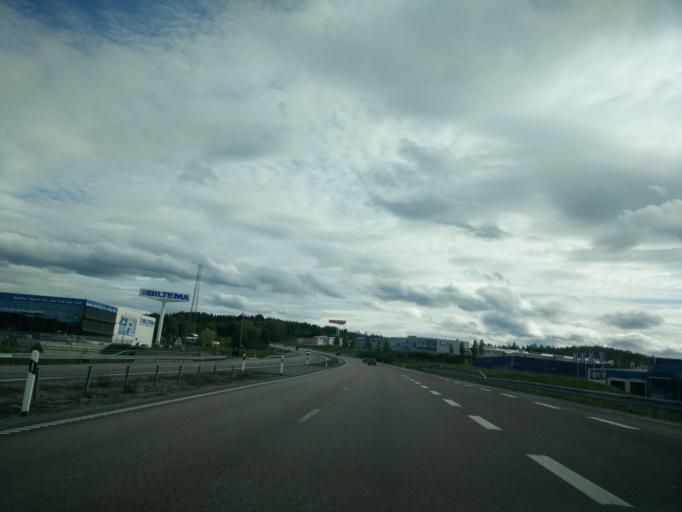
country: SE
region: Vaesternorrland
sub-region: Sundsvalls Kommun
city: Sundsbruk
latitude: 62.4447
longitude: 17.3381
